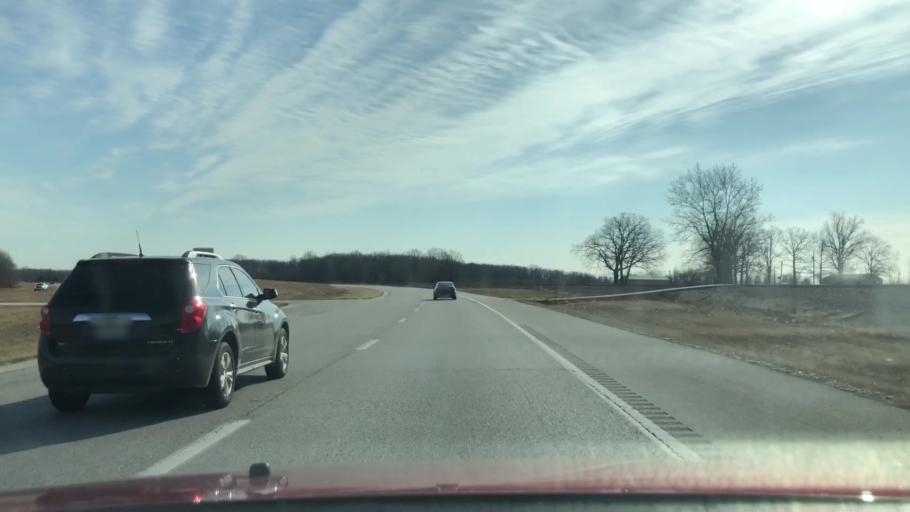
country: US
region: Missouri
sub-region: Webster County
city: Seymour
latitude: 37.1320
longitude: -92.7411
